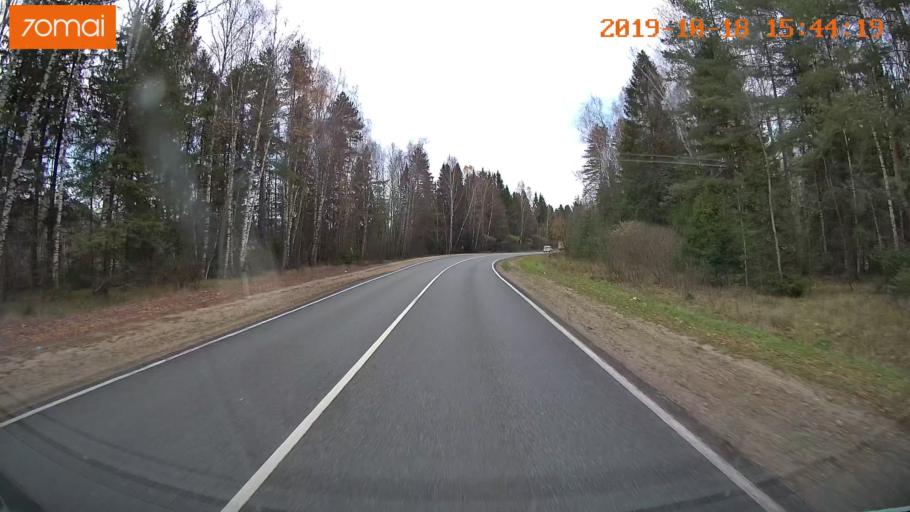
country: RU
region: Vladimir
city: Golovino
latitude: 55.9801
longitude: 40.5484
